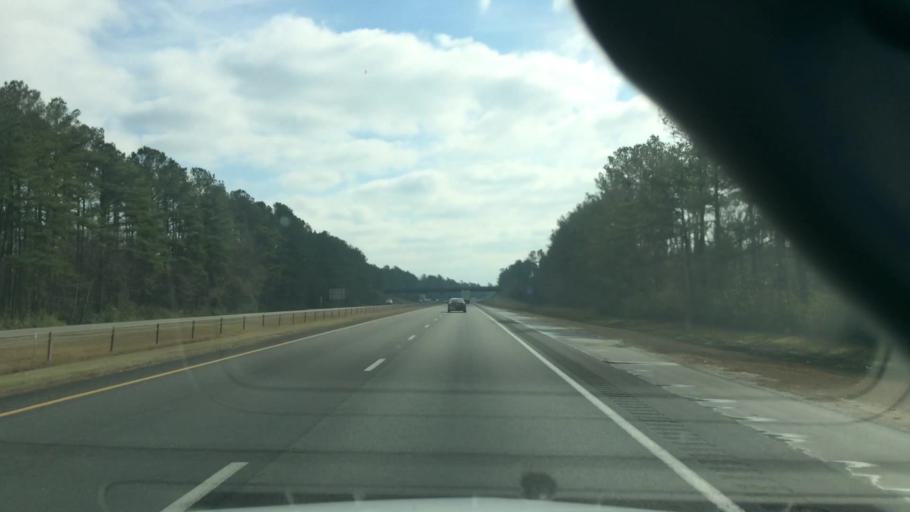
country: US
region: North Carolina
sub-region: Pender County
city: Burgaw
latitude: 34.5693
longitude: -77.8993
